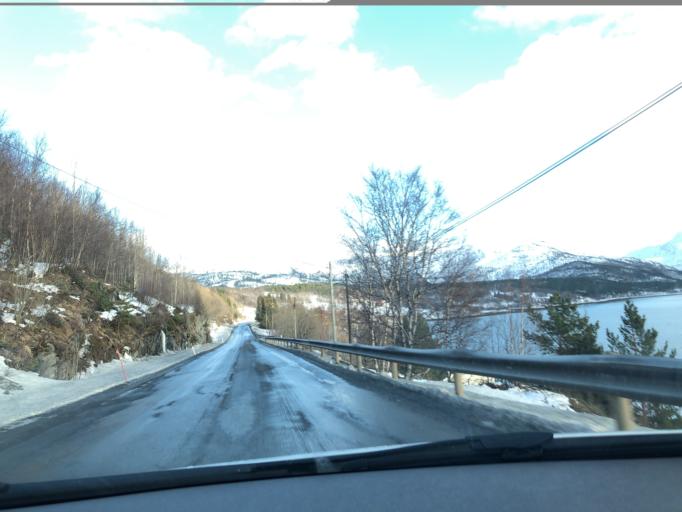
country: NO
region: Nordland
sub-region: Narvik
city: Bjerkvik
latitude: 68.4642
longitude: 17.6693
